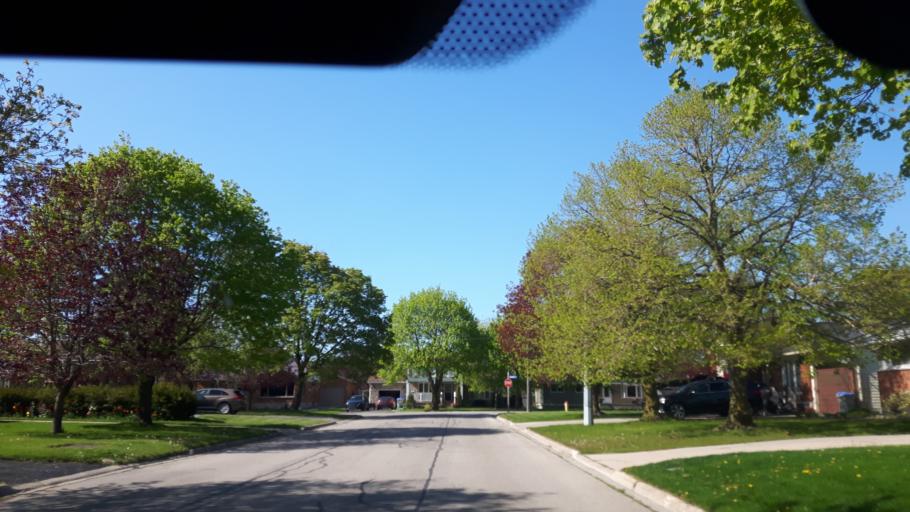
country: CA
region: Ontario
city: Goderich
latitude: 43.7310
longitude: -81.7200
